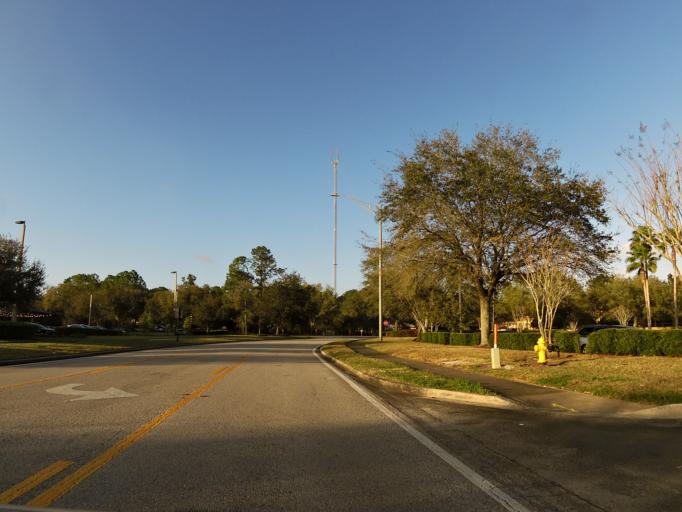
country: US
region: Florida
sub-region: Duval County
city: Jacksonville
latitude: 30.2672
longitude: -81.5547
